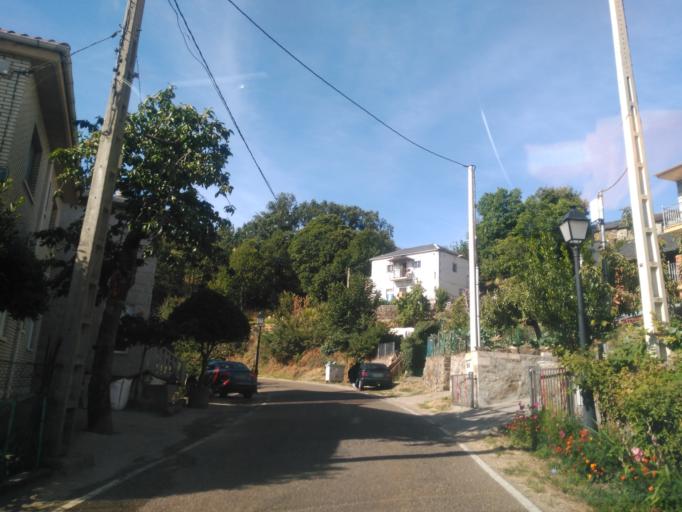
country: ES
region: Castille and Leon
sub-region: Provincia de Zamora
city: Cobreros
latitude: 42.1335
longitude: -6.7225
